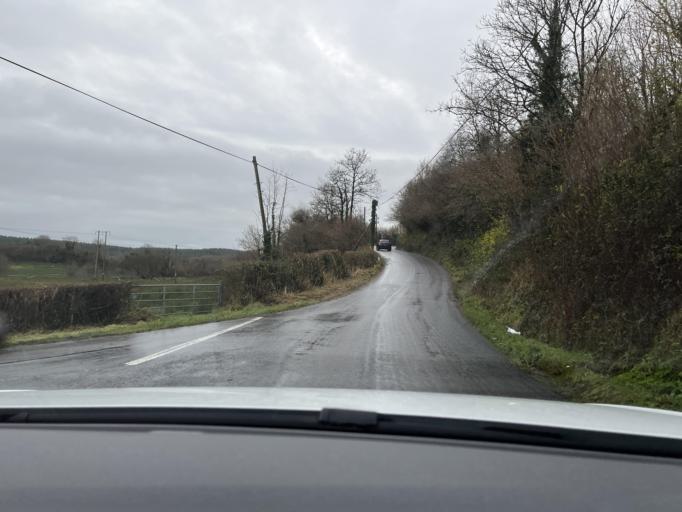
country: IE
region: Connaught
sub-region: County Leitrim
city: Manorhamilton
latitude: 54.2515
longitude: -8.2425
